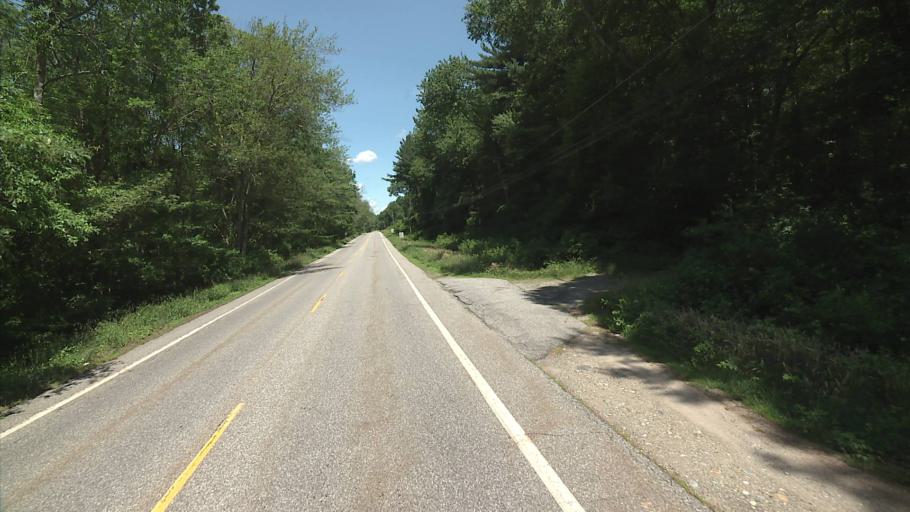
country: US
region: Connecticut
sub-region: New London County
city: Preston City
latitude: 41.4712
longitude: -71.9035
